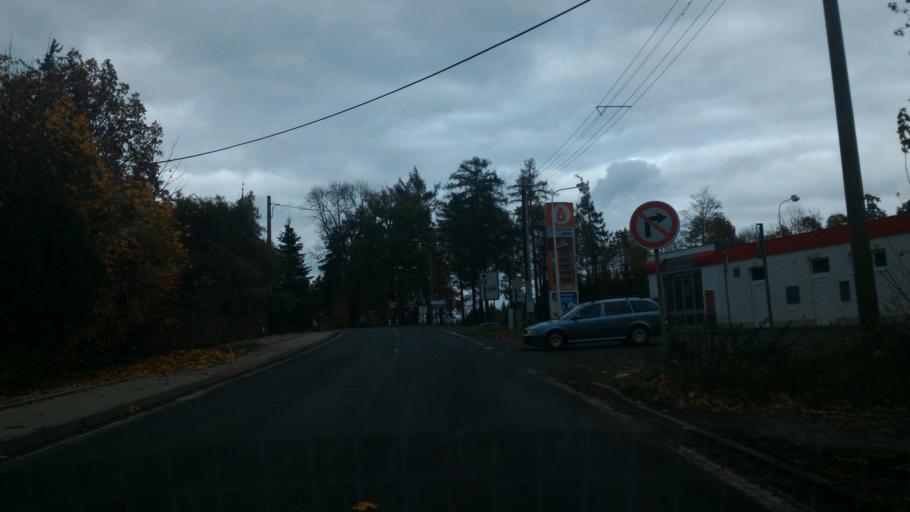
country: CZ
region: Ustecky
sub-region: Okres Decin
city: Rumburk
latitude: 50.9680
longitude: 14.5630
